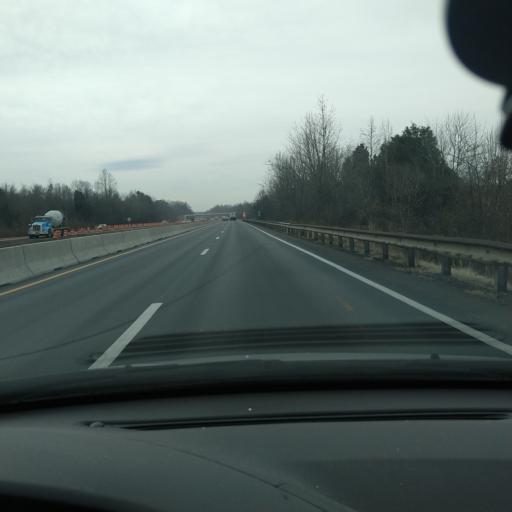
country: US
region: North Carolina
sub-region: Rowan County
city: China Grove
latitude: 35.5469
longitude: -80.5725
